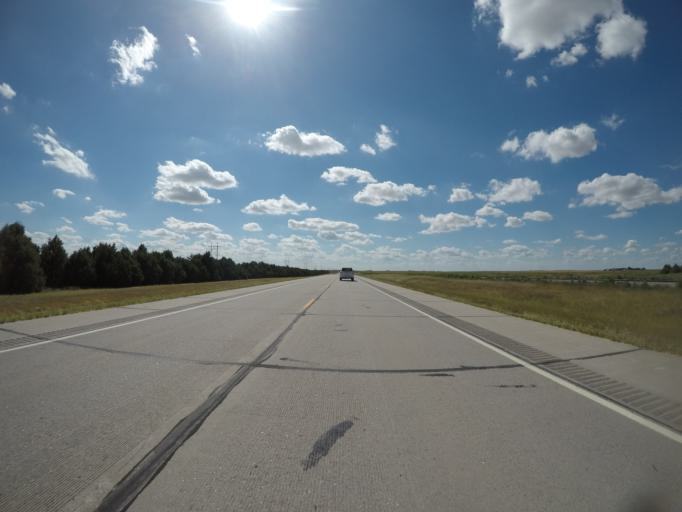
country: US
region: Colorado
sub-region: Phillips County
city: Holyoke
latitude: 40.5991
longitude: -102.3921
